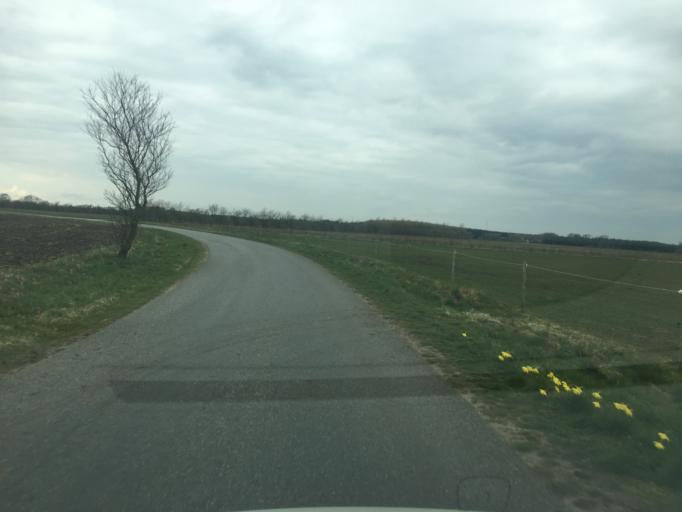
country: DK
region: South Denmark
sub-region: Aabenraa Kommune
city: Tinglev
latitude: 55.0446
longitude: 9.1458
